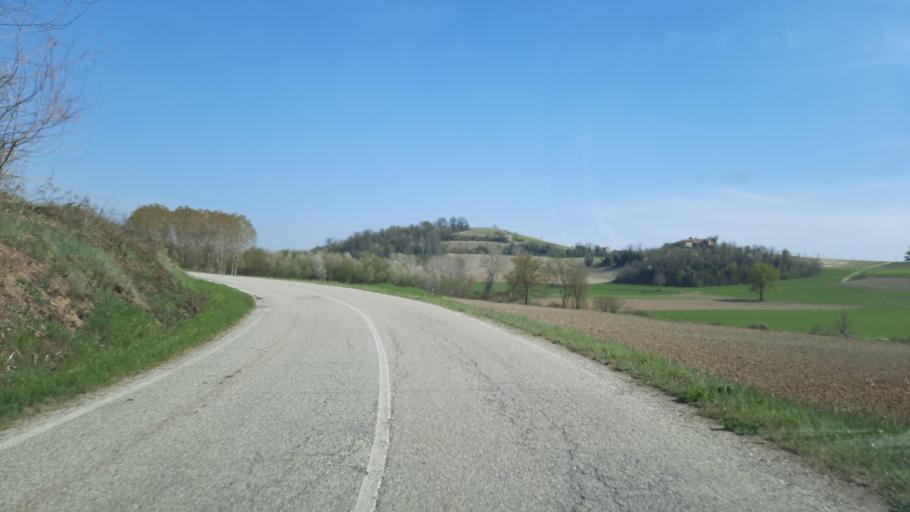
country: IT
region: Piedmont
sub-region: Provincia di Alessandria
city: Olivola
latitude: 45.0301
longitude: 8.3666
